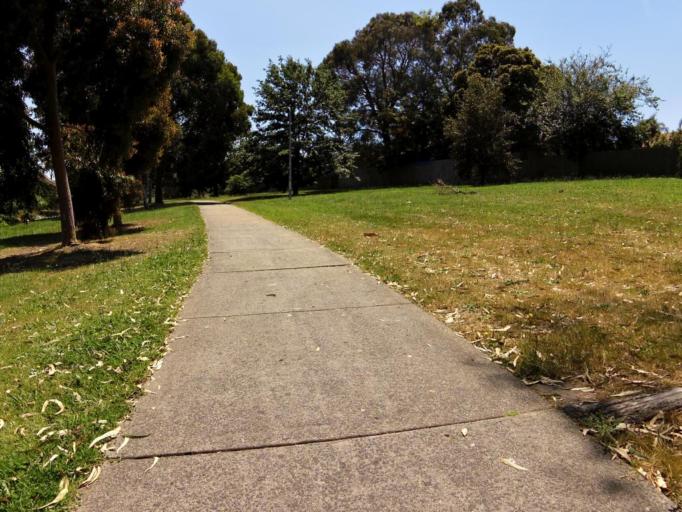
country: AU
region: Victoria
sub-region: Casey
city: Endeavour Hills
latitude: -37.9807
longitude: 145.2620
